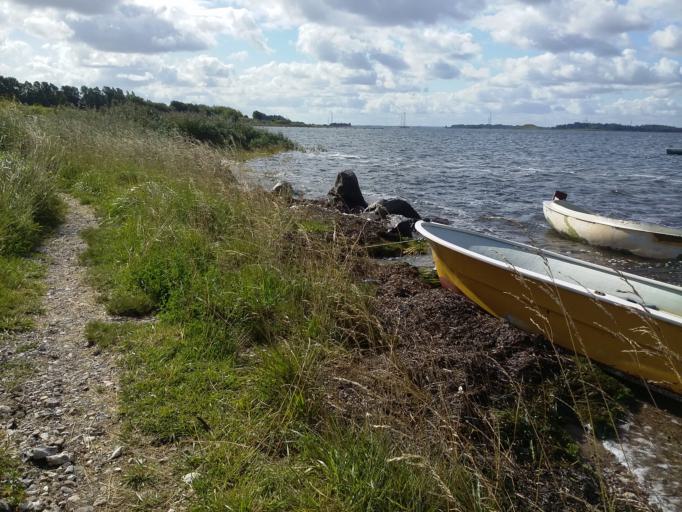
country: DK
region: Capital Region
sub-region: Frederikssund Kommune
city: Frederikssund
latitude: 55.8224
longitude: 12.0638
